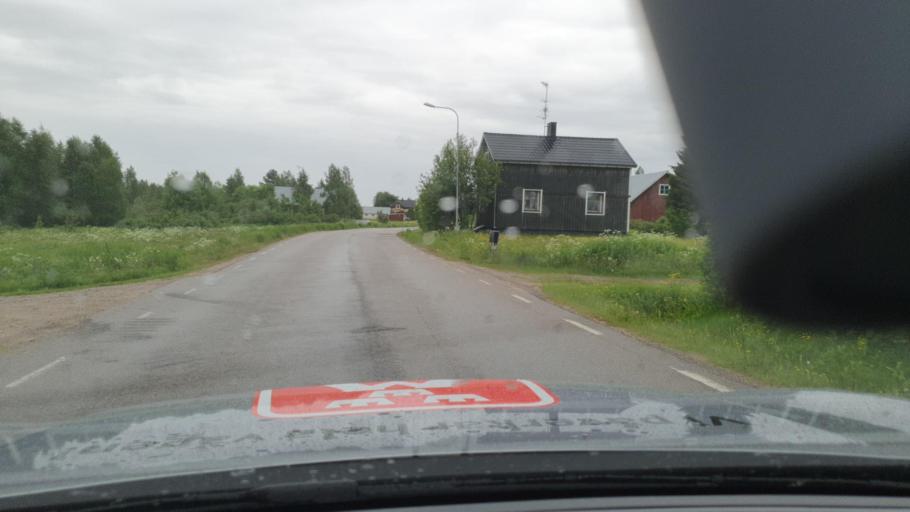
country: SE
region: Norrbotten
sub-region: Pajala Kommun
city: Pajala
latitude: 66.7976
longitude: 23.1237
